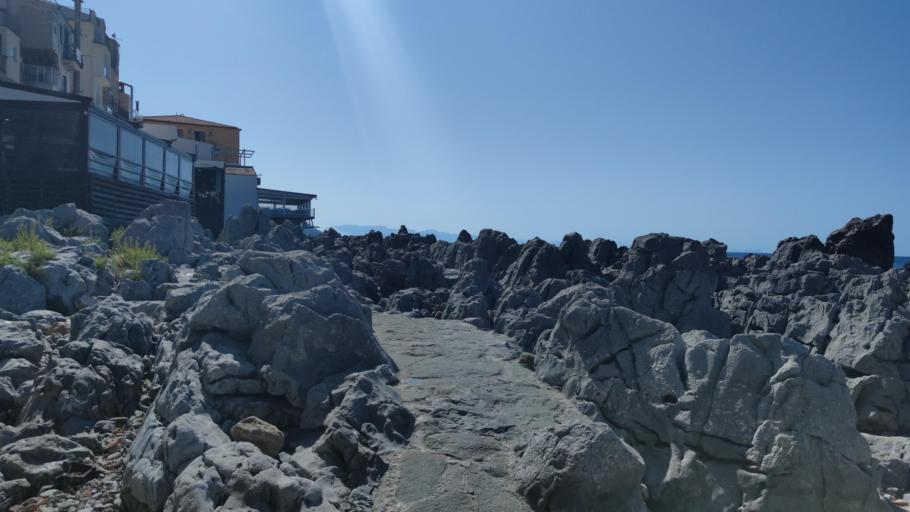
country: IT
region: Sicily
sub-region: Palermo
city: Cefalu
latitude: 38.0411
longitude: 14.0211
